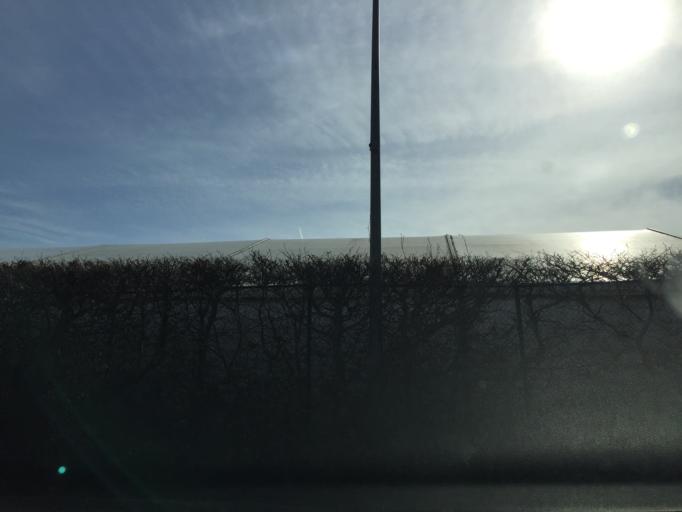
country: JE
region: St Helier
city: Saint Helier
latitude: 49.2188
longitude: -2.1402
